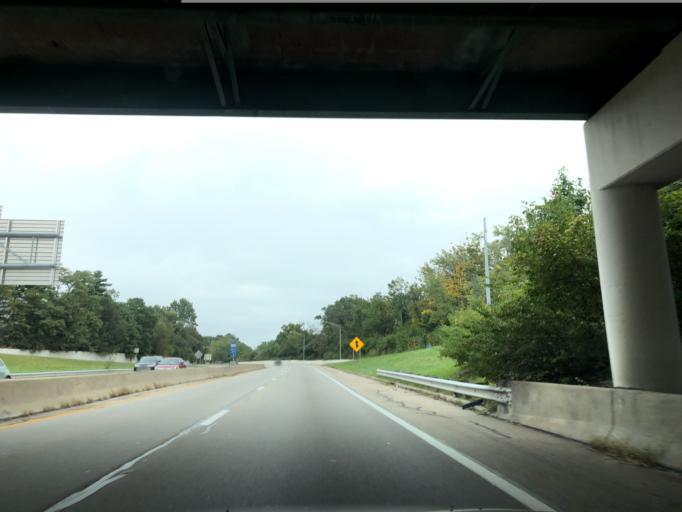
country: US
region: Ohio
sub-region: Hamilton County
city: Amberley
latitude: 39.2167
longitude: -84.4269
